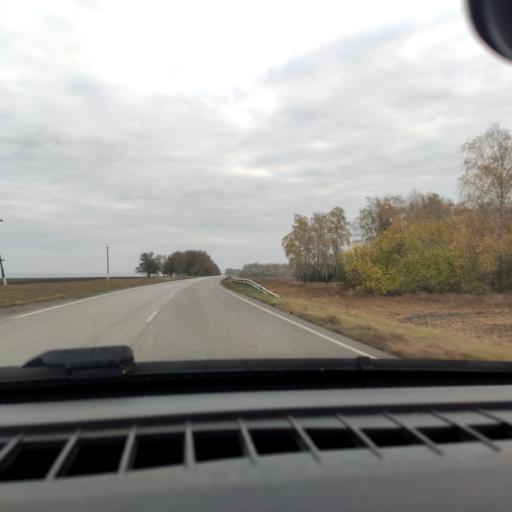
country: RU
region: Belgorod
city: Ilovka
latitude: 50.7561
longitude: 38.7260
